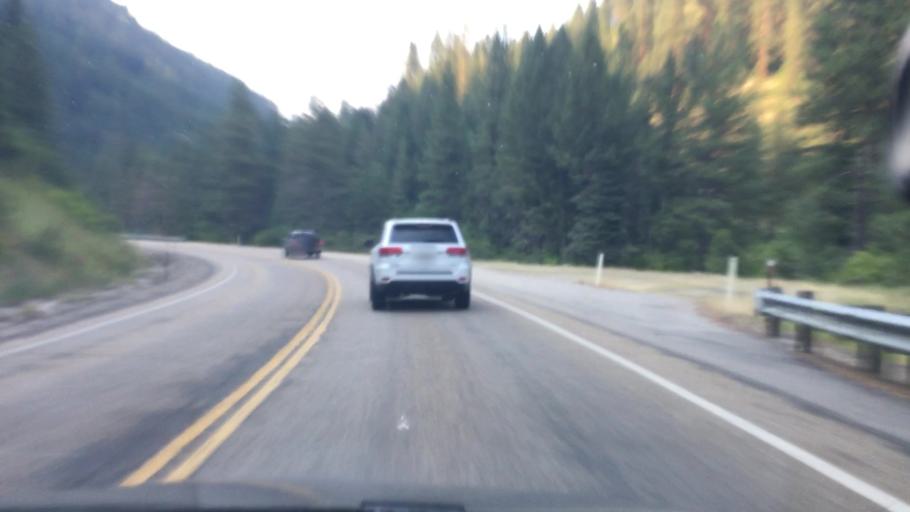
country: US
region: Idaho
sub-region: Valley County
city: Cascade
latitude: 44.1941
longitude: -116.1122
